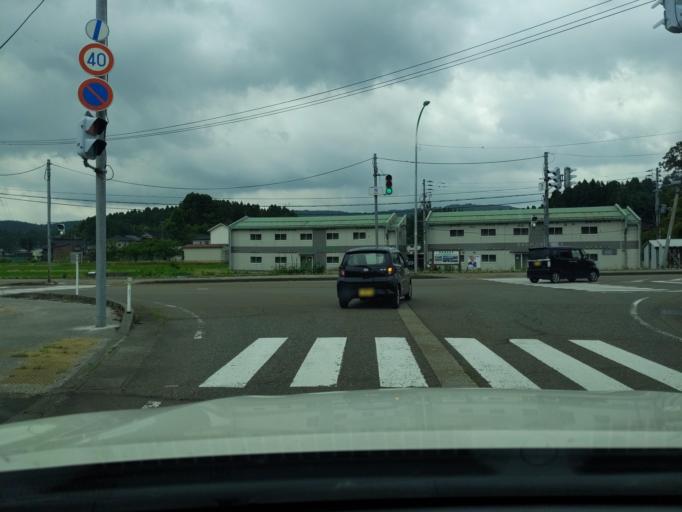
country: JP
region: Niigata
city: Kashiwazaki
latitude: 37.3319
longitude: 138.5767
